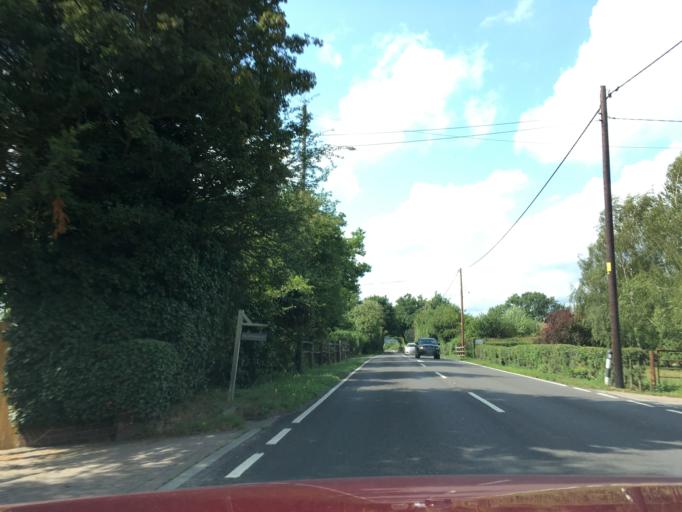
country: GB
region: England
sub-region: Kent
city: Headcorn
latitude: 51.1935
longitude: 0.6009
